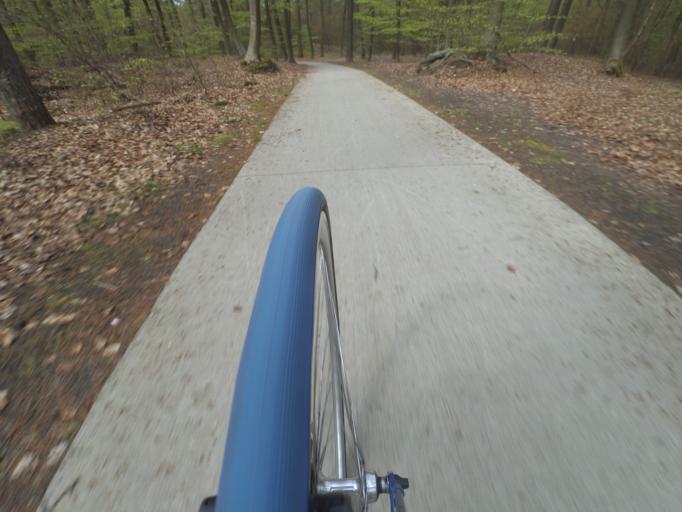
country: NL
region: Gelderland
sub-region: Gemeente Nunspeet
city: Nunspeet
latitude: 52.3653
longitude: 5.7564
